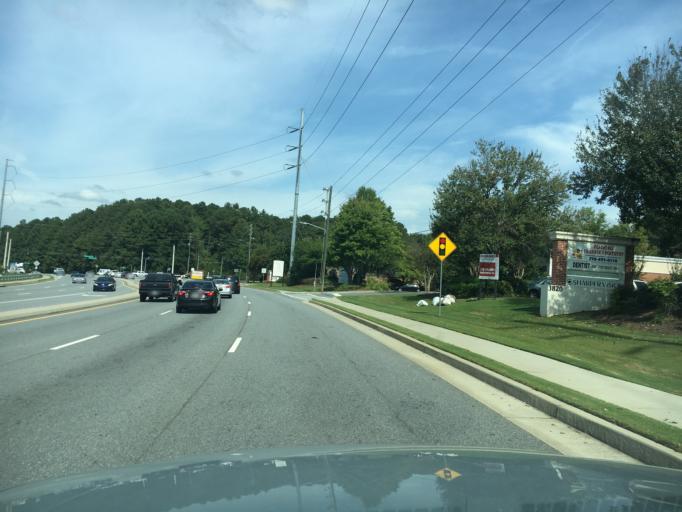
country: US
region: Georgia
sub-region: Gwinnett County
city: Duluth
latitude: 34.0007
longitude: -84.1615
